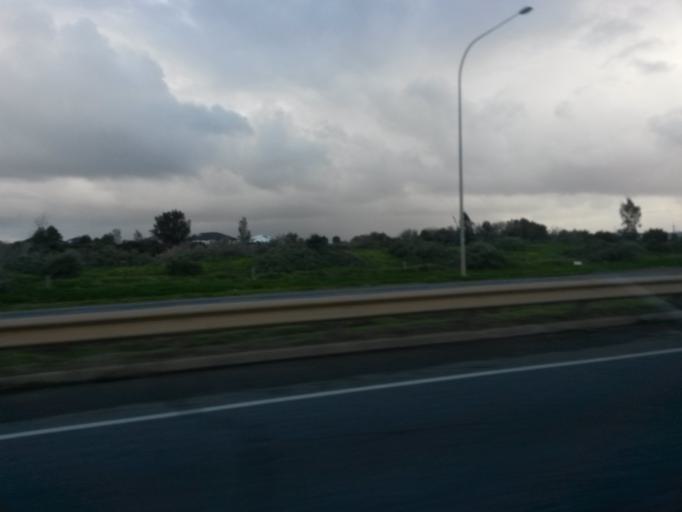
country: AU
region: South Australia
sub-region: Salisbury
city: Ingle Farm
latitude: -34.8090
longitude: 138.5998
